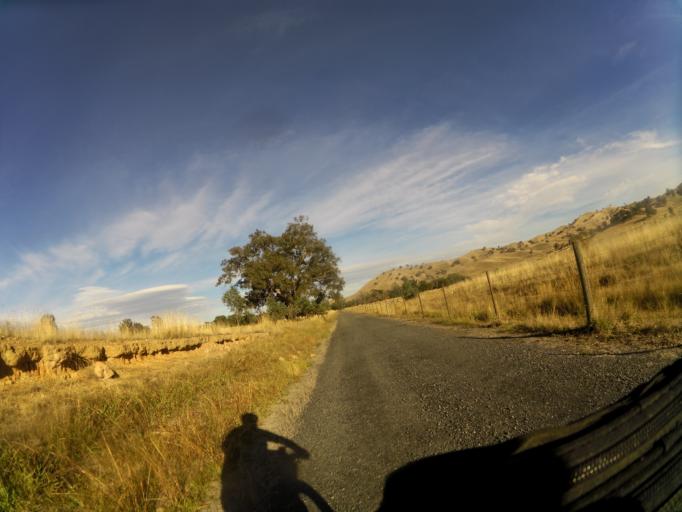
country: AU
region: Victoria
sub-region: Murrindindi
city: Alexandra
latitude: -37.0240
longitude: 145.8421
